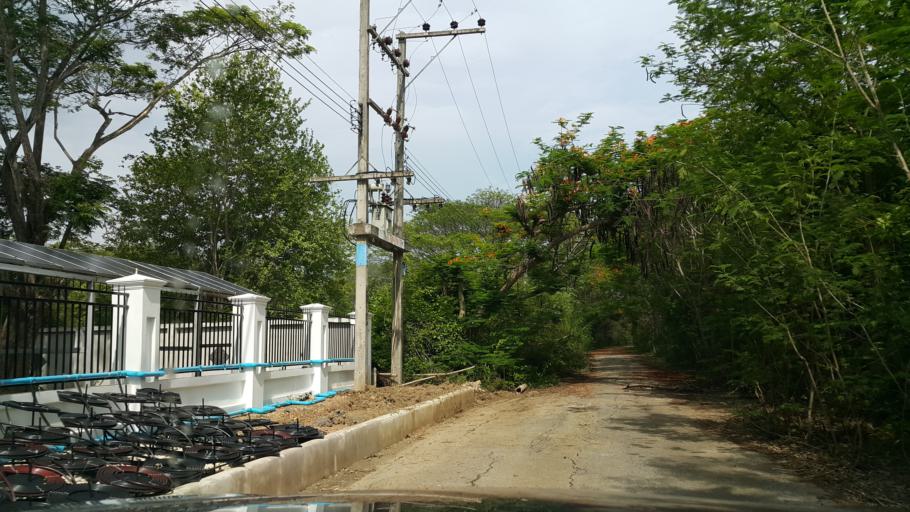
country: TH
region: Chiang Mai
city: San Kamphaeng
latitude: 18.7600
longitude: 99.1159
